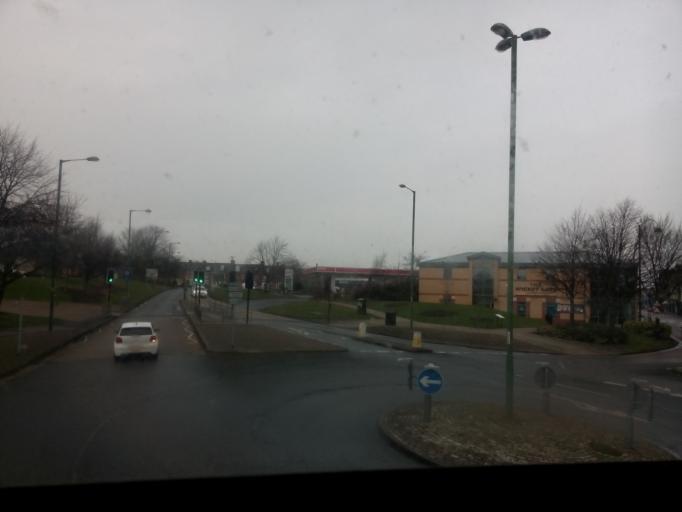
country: GB
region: England
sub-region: County Durham
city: Chester-le-Street
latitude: 54.8514
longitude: -1.5733
